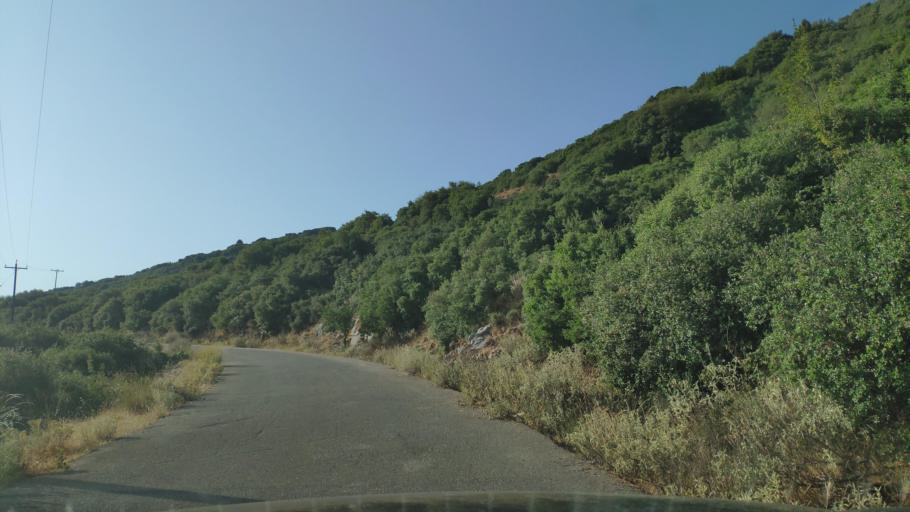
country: GR
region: West Greece
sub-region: Nomos Aitolias kai Akarnanias
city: Monastirakion
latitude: 38.8429
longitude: 20.9765
